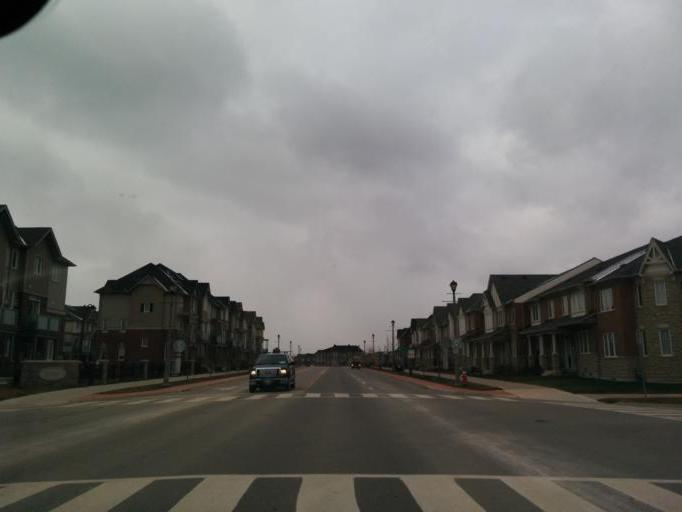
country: CA
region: Ontario
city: Brampton
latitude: 43.7544
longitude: -79.8246
